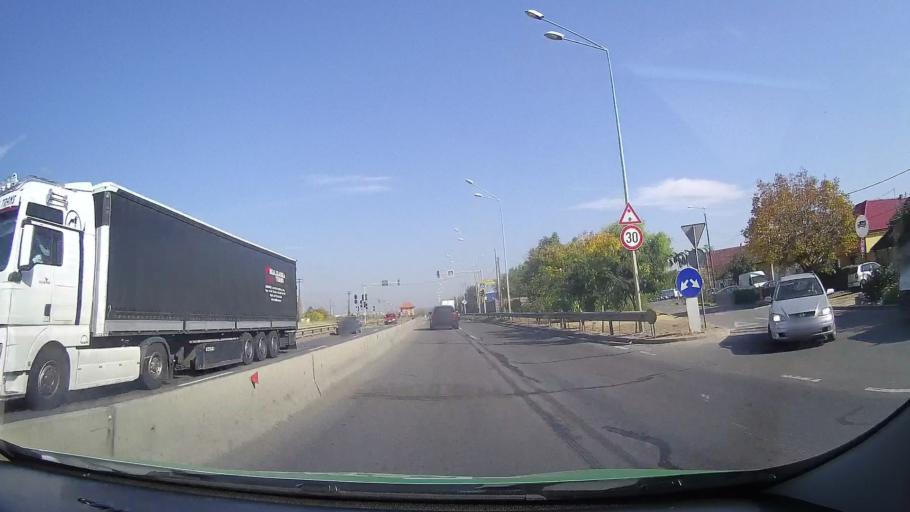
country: RO
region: Bihor
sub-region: Comuna Biharea
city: Oradea
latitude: 47.0607
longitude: 21.8950
